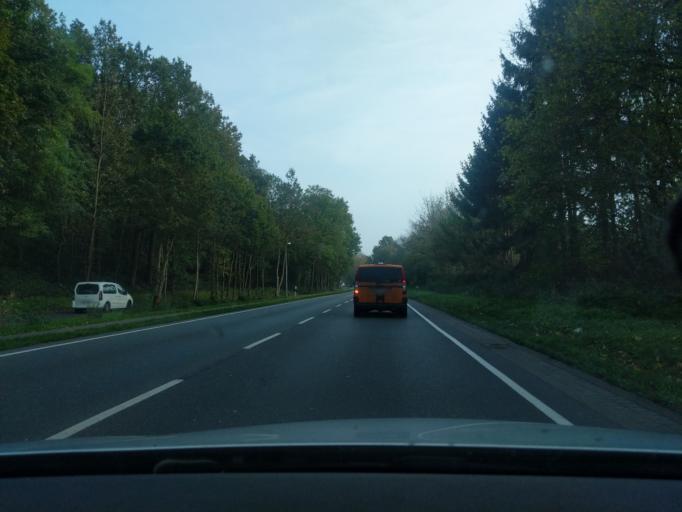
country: DE
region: Lower Saxony
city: Stade
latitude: 53.5925
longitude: 9.4419
